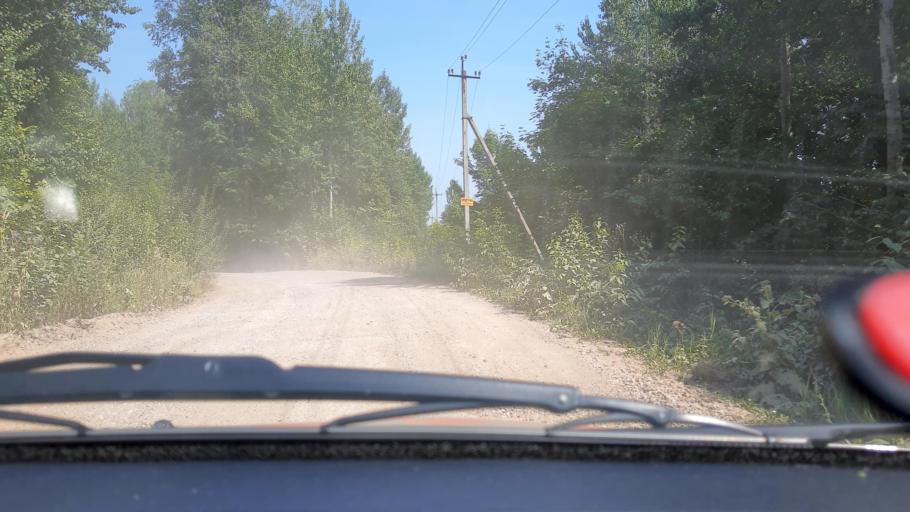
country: RU
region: Bashkortostan
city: Karmaskaly
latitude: 54.3898
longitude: 55.8944
